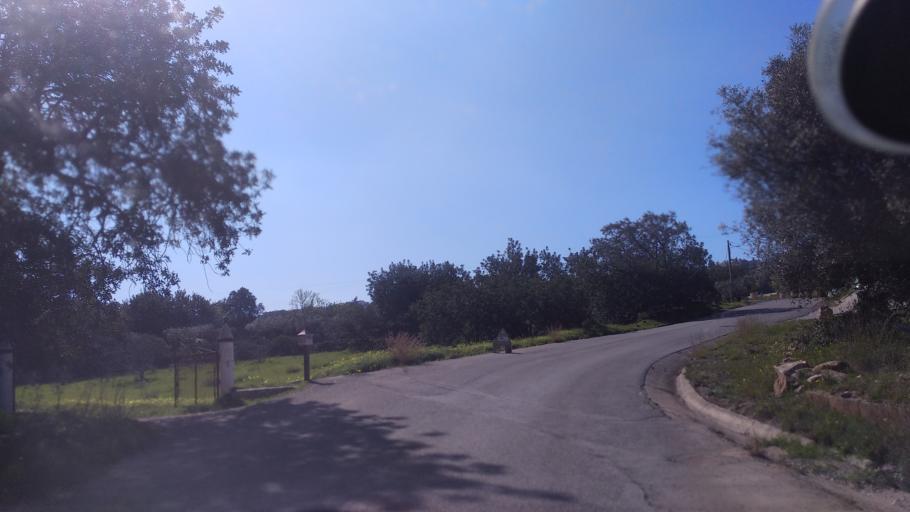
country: PT
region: Faro
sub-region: Faro
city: Santa Barbara de Nexe
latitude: 37.1192
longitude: -7.9250
